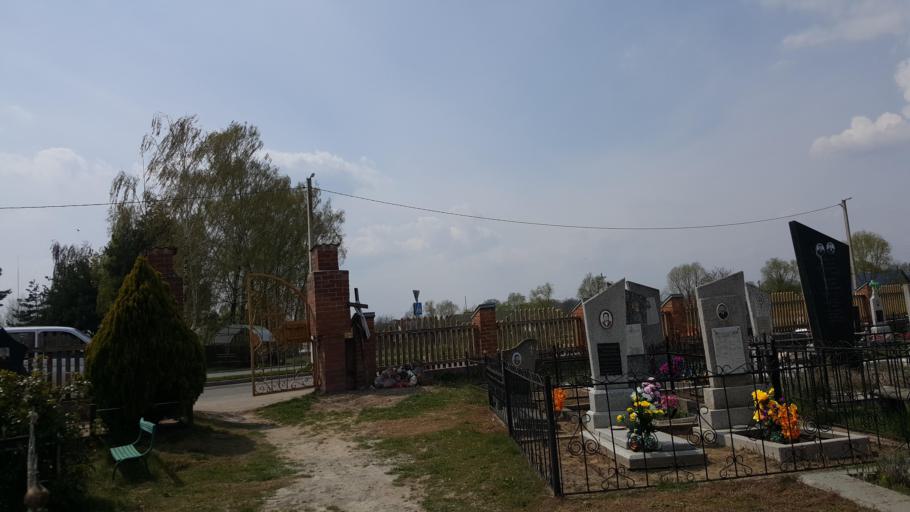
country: BY
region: Brest
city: Zhabinka
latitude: 52.2008
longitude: 24.0276
